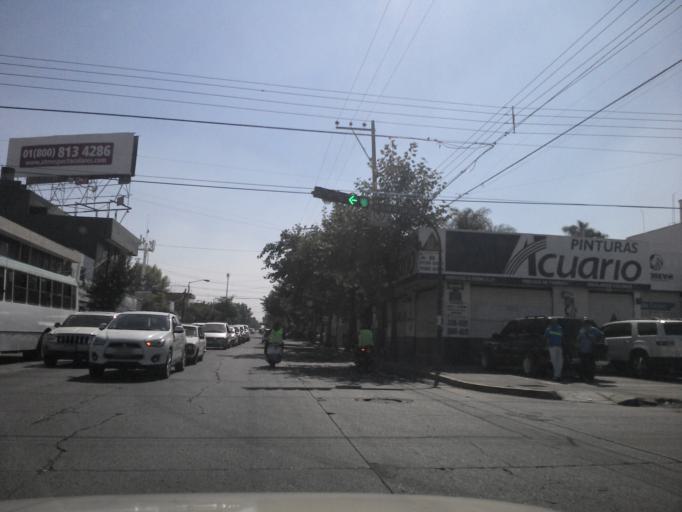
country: MX
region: Jalisco
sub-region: Zapopan
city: Zapopan
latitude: 20.6970
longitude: -103.3582
